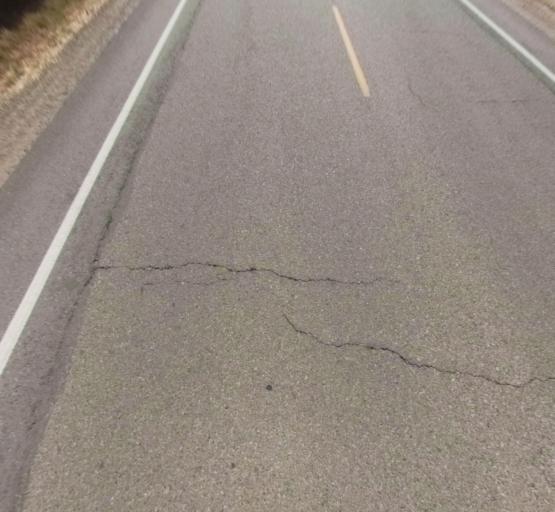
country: US
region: California
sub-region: Madera County
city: Chowchilla
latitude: 37.1127
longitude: -120.3726
